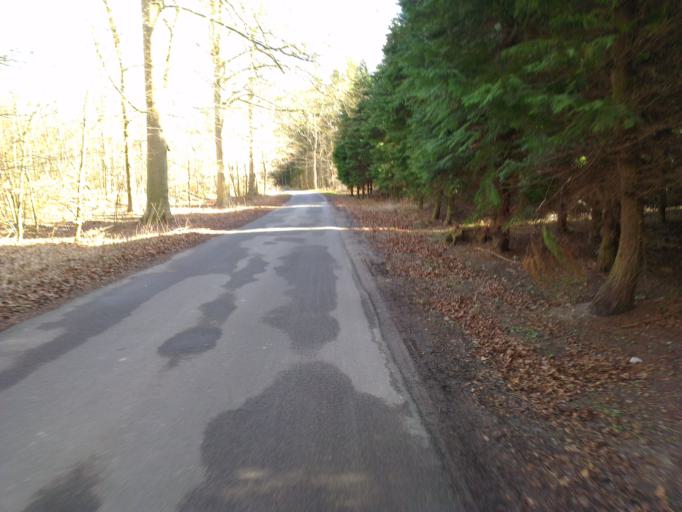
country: DK
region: Zealand
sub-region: Roskilde Kommune
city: Jyllinge
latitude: 55.7360
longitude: 12.0540
